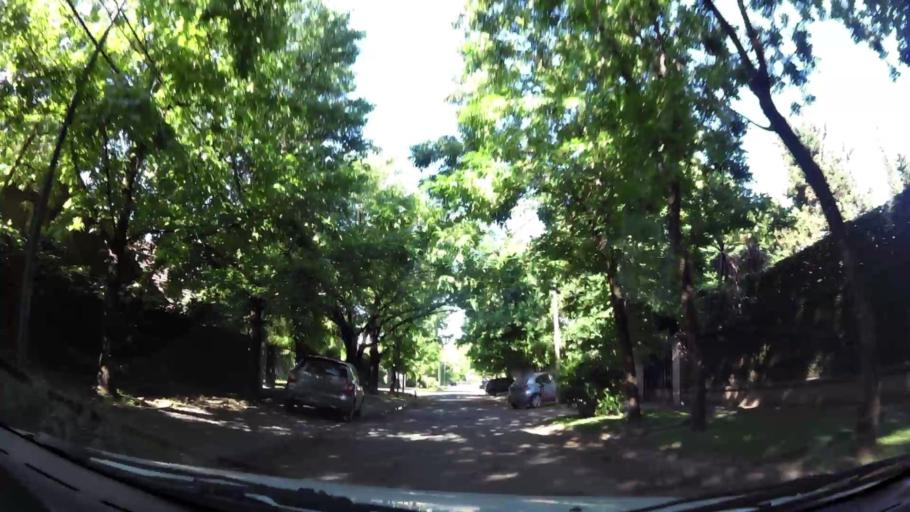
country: AR
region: Buenos Aires
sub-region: Partido de San Isidro
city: San Isidro
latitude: -34.4857
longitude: -58.5427
